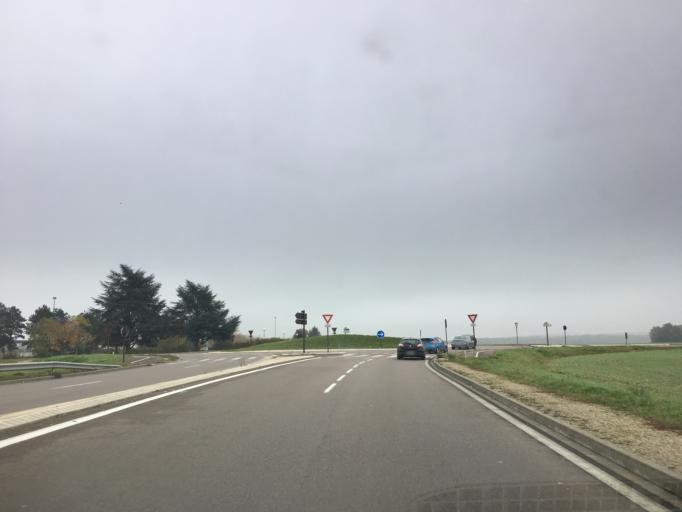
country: FR
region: Ile-de-France
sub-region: Departement de Seine-et-Marne
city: Cannes-Ecluse
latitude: 48.3577
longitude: 2.9829
